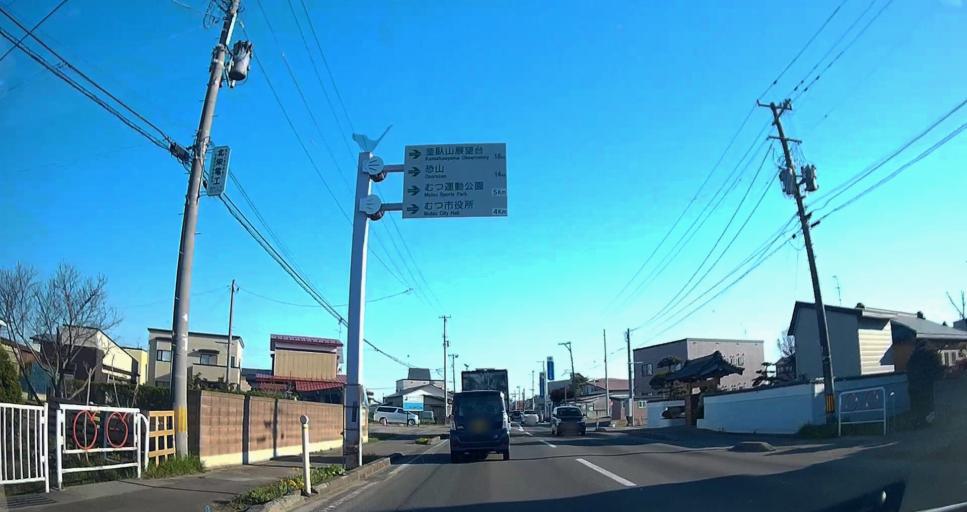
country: JP
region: Aomori
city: Mutsu
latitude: 41.2983
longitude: 141.2216
